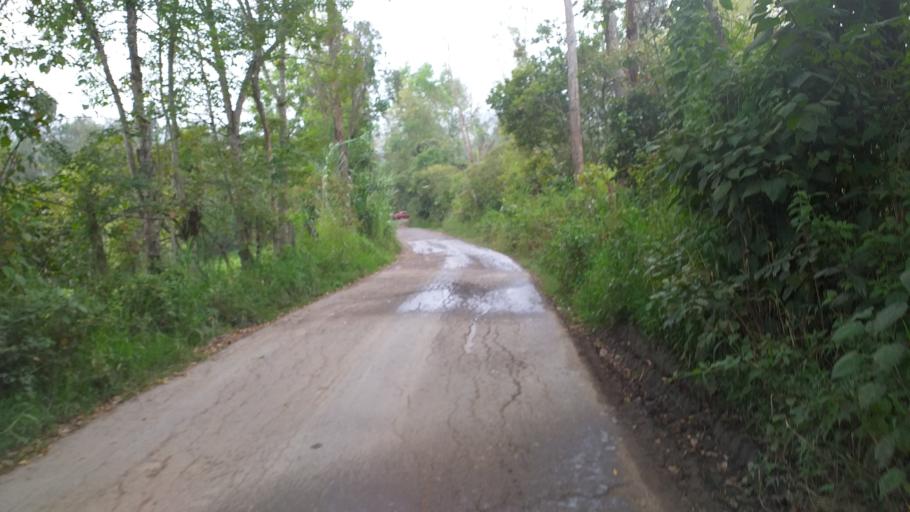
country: CO
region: Cundinamarca
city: Tenza
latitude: 5.0946
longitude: -73.4501
